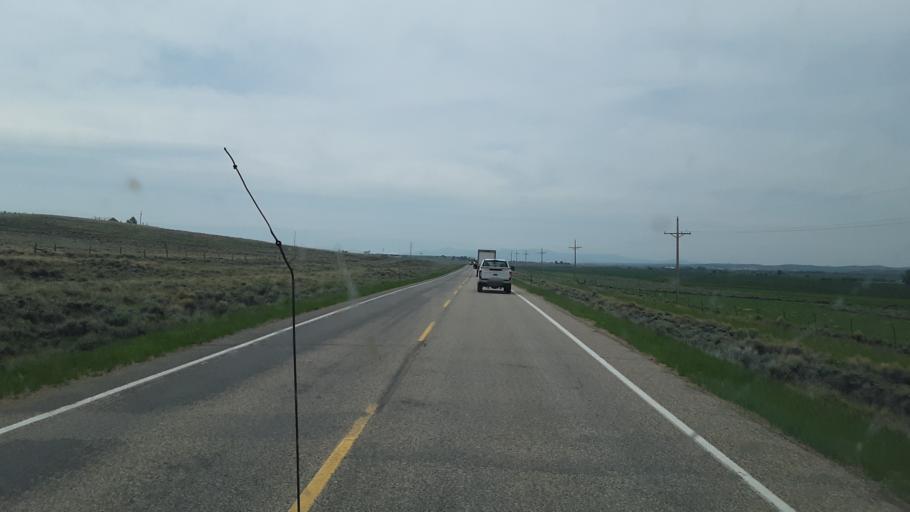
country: US
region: Colorado
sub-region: Jackson County
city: Walden
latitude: 40.7713
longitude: -106.2816
